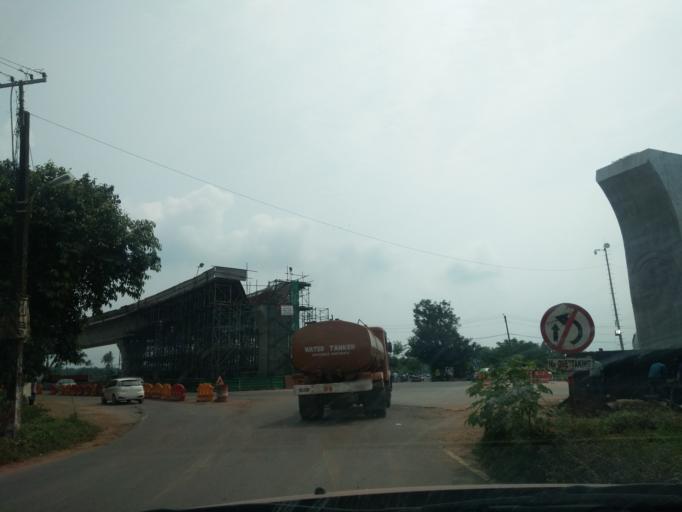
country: IN
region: Goa
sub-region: North Goa
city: Panaji
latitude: 15.4915
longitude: 73.8439
